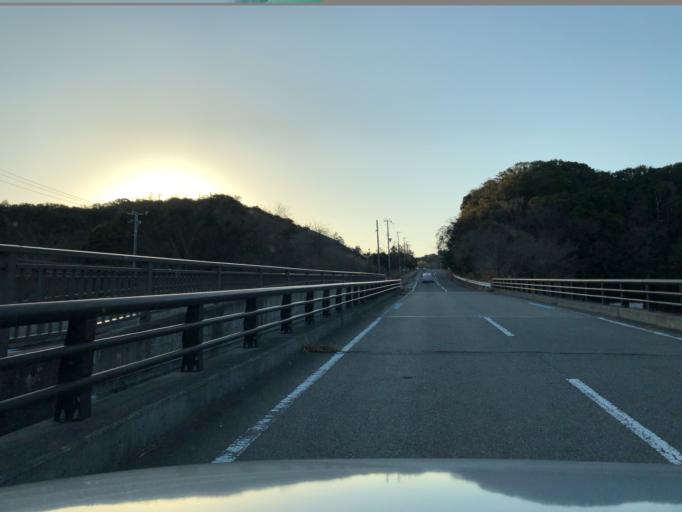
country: JP
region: Wakayama
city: Tanabe
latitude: 33.6613
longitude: 135.3822
